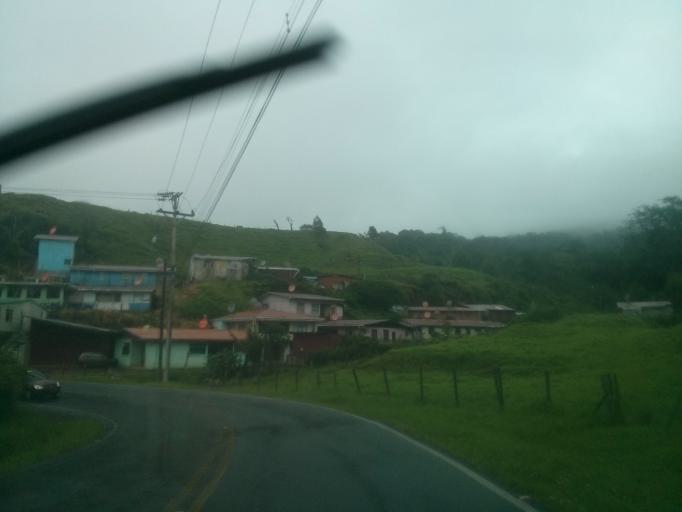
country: CR
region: Alajuela
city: Sabanilla
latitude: 10.1666
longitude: -84.1923
